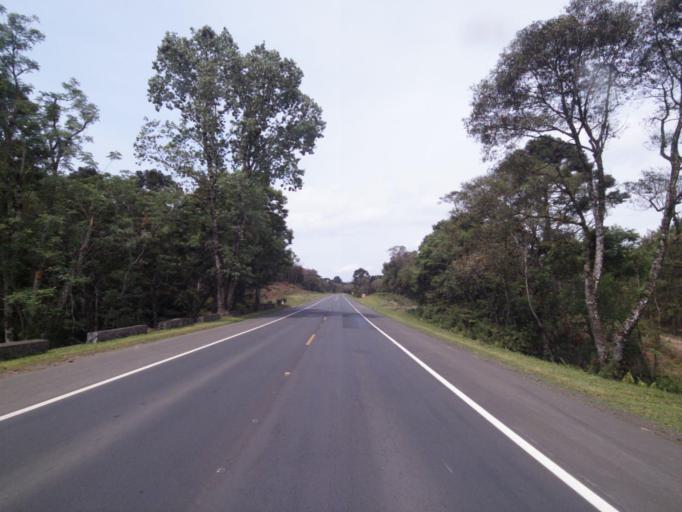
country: BR
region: Parana
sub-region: Irati
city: Irati
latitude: -25.4667
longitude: -50.5172
